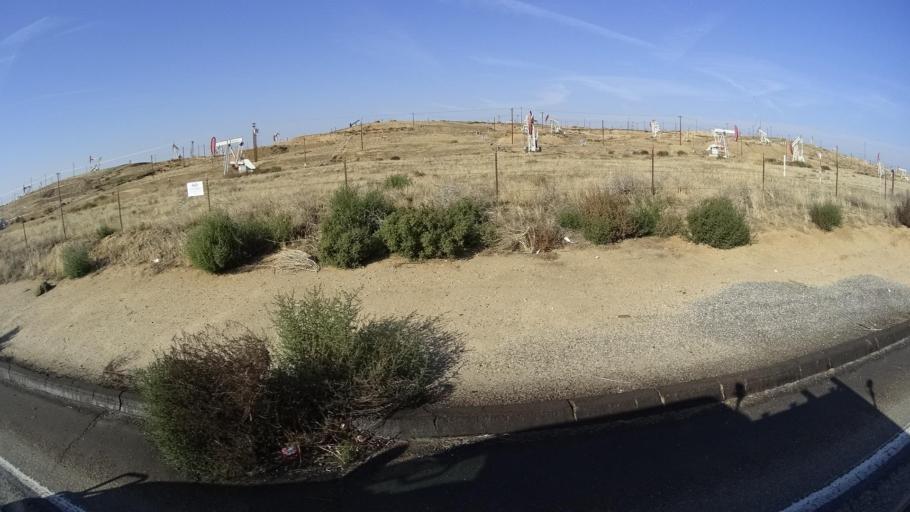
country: US
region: California
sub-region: Kern County
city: Oildale
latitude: 35.4677
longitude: -119.0249
